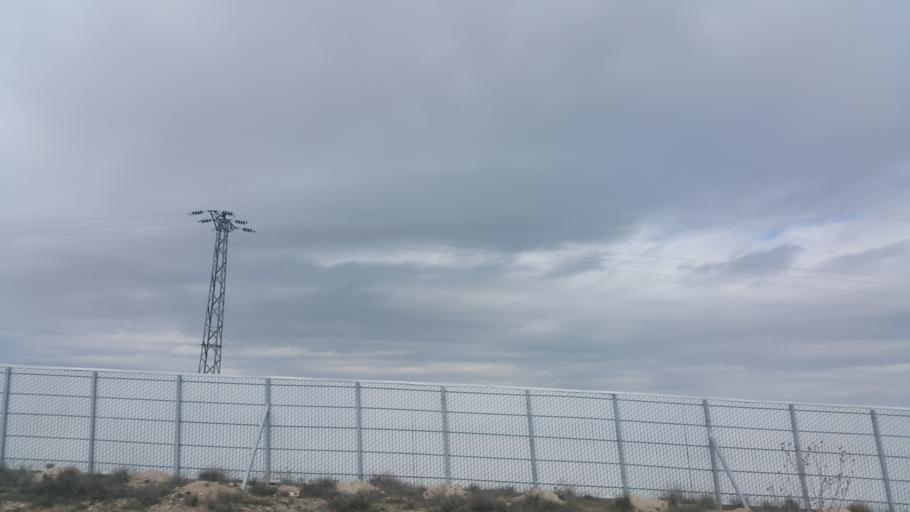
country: TR
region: Nigde
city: Altunhisar
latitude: 37.8923
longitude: 34.1387
